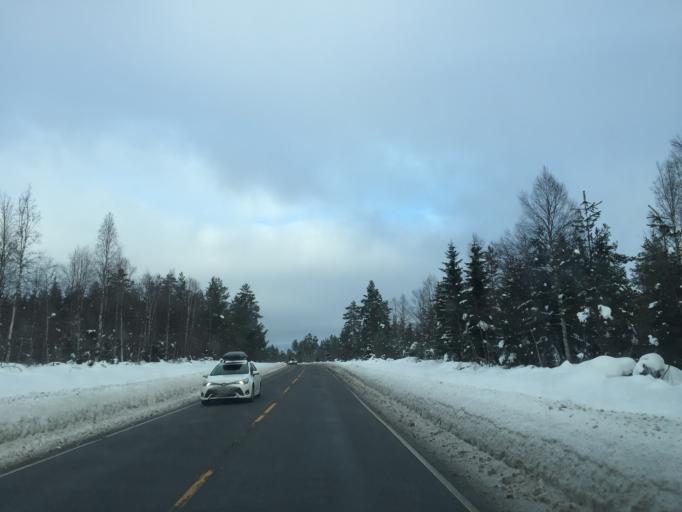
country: NO
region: Hedmark
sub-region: Trysil
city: Innbygda
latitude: 61.1414
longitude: 12.1199
